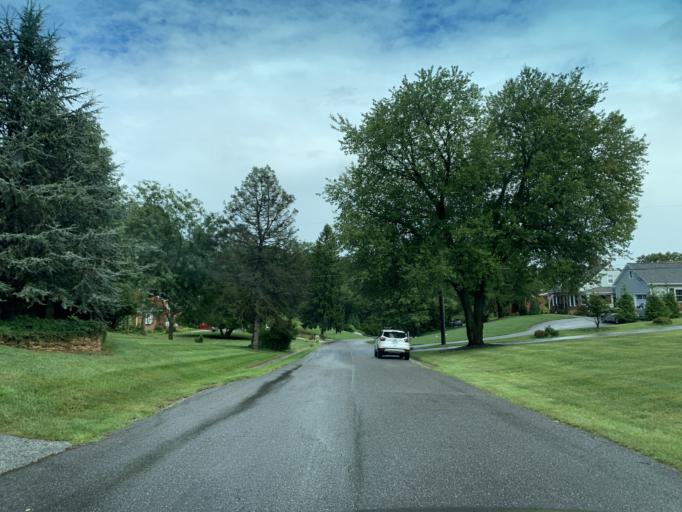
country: US
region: Maryland
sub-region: Baltimore County
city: Timonium
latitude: 39.4480
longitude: -76.6246
